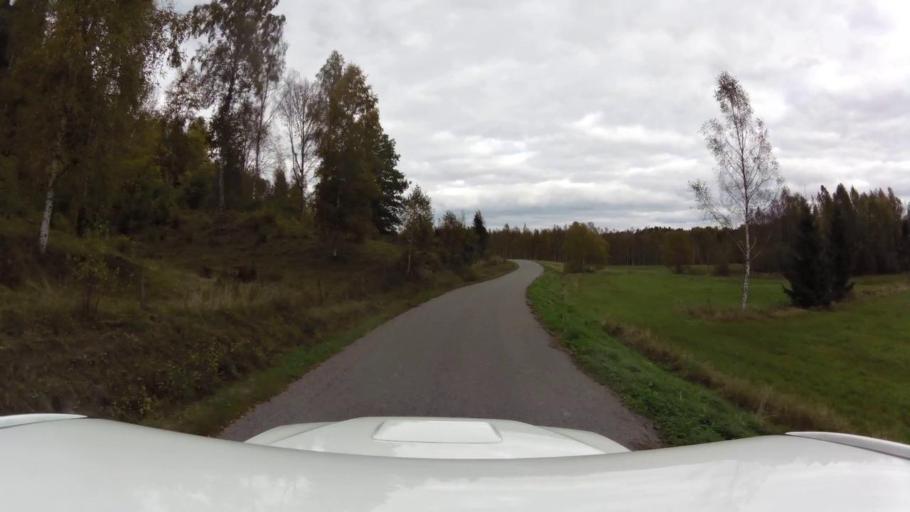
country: SE
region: OEstergoetland
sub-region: Kinda Kommun
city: Rimforsa
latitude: 58.1977
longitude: 15.5621
